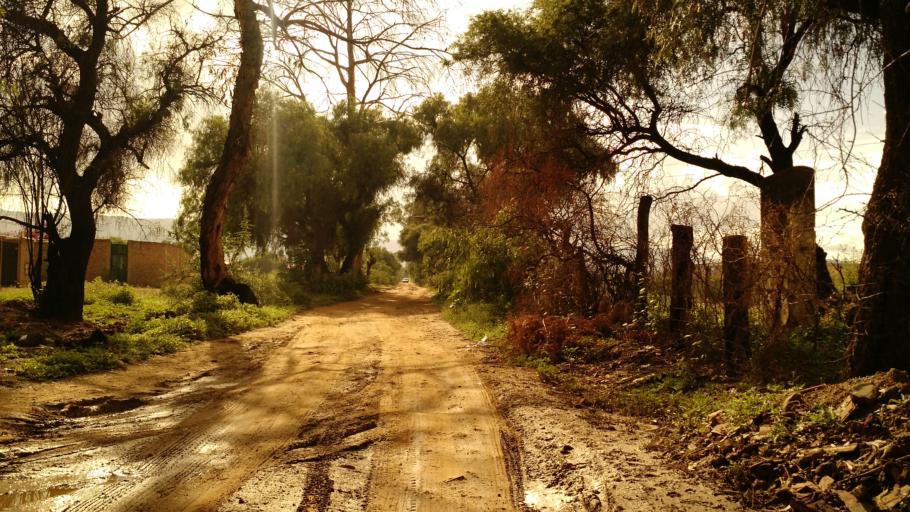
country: BO
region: Cochabamba
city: Cochabamba
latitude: -17.4544
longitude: -66.1498
